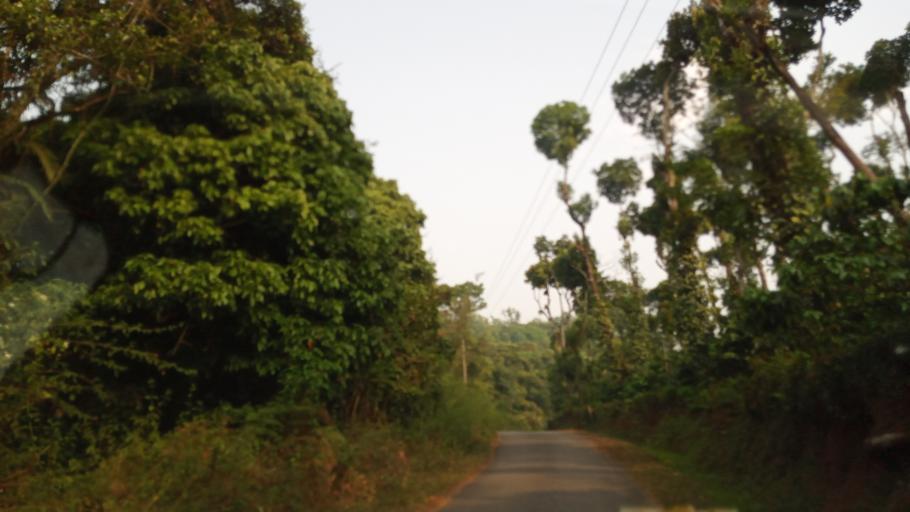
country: IN
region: Karnataka
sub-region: Chikmagalur
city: Mudigere
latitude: 13.0119
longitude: 75.6280
